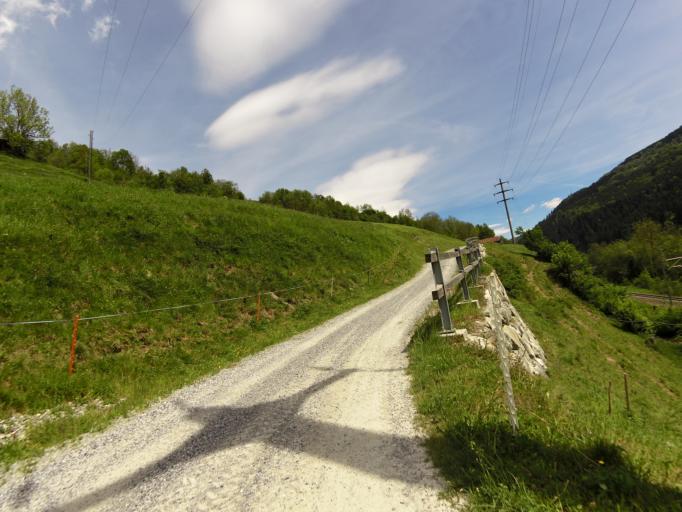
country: CH
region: Grisons
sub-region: Surselva District
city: Trun
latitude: 46.7458
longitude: 9.0152
